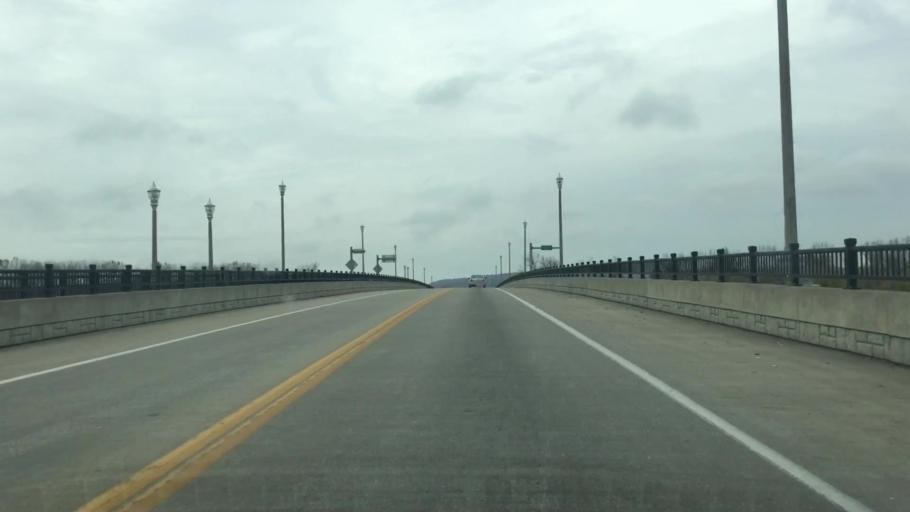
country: US
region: Missouri
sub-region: Gasconade County
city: Hermann
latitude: 38.7082
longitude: -91.4382
